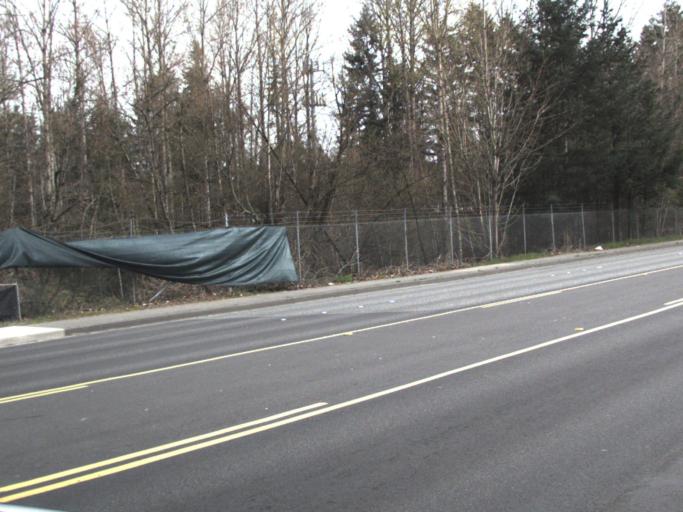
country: US
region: Washington
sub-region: King County
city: Covington
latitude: 47.3580
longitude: -122.1273
